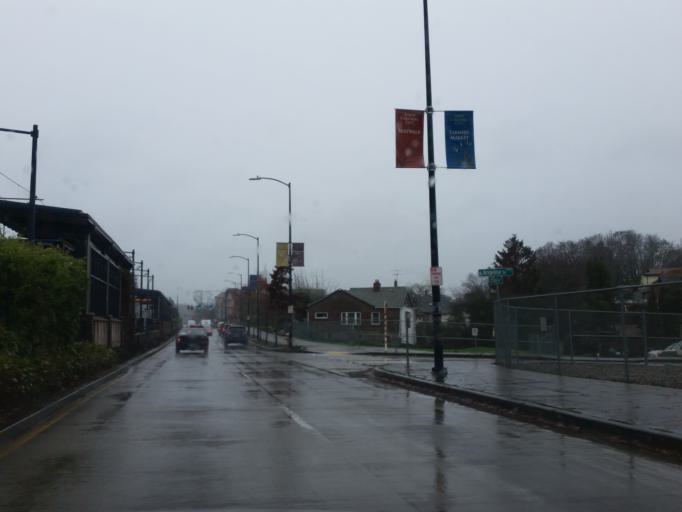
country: US
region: Washington
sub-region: King County
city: Seattle
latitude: 47.5590
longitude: -122.2921
